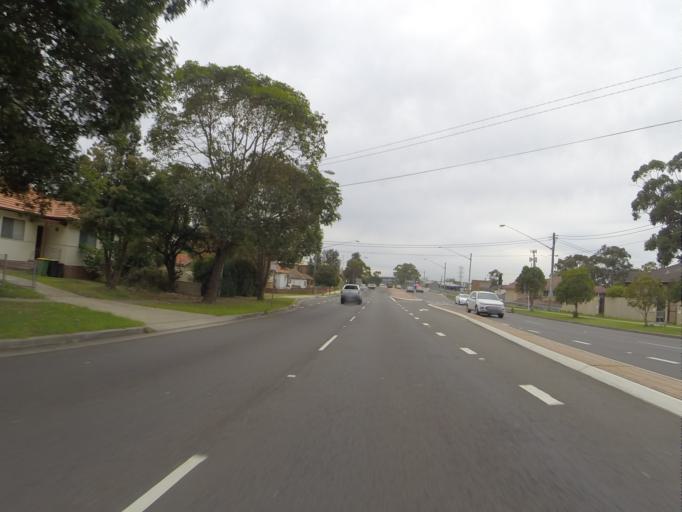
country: AU
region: New South Wales
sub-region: Bankstown
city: Padstow
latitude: -33.9497
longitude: 151.0380
